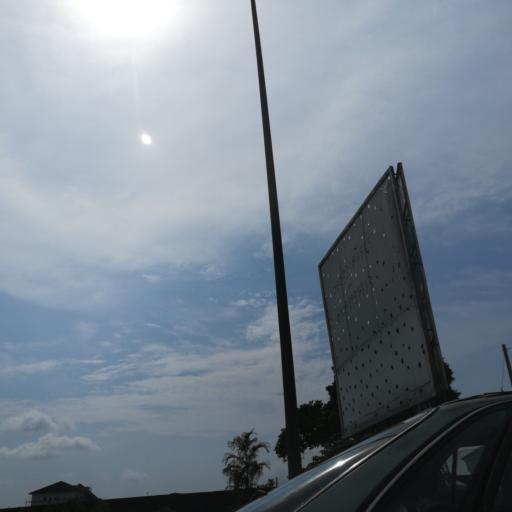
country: NG
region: Rivers
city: Port Harcourt
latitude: 4.8567
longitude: 7.0228
